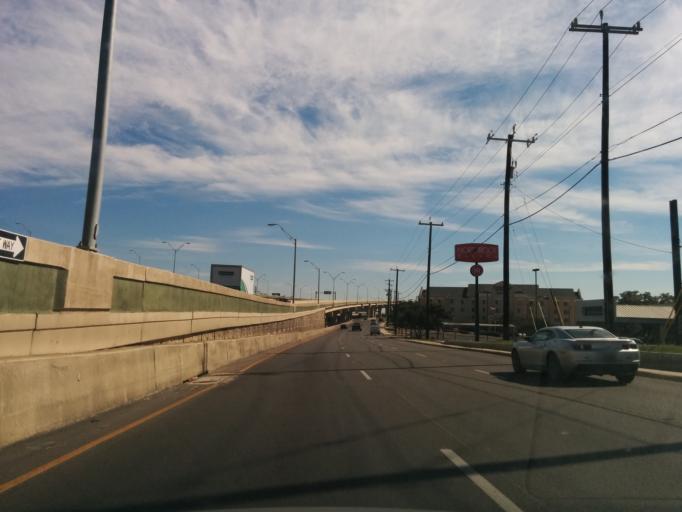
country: US
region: Texas
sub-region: Bexar County
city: Hollywood Park
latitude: 29.6100
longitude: -98.4771
